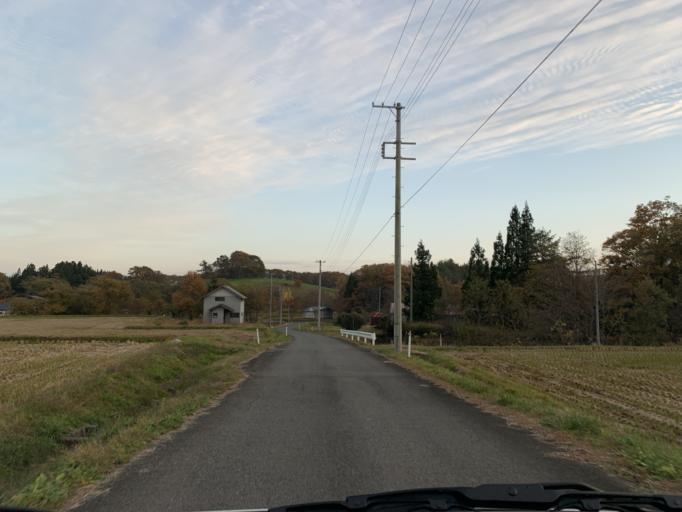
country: JP
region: Iwate
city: Ichinoseki
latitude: 38.9934
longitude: 141.0140
